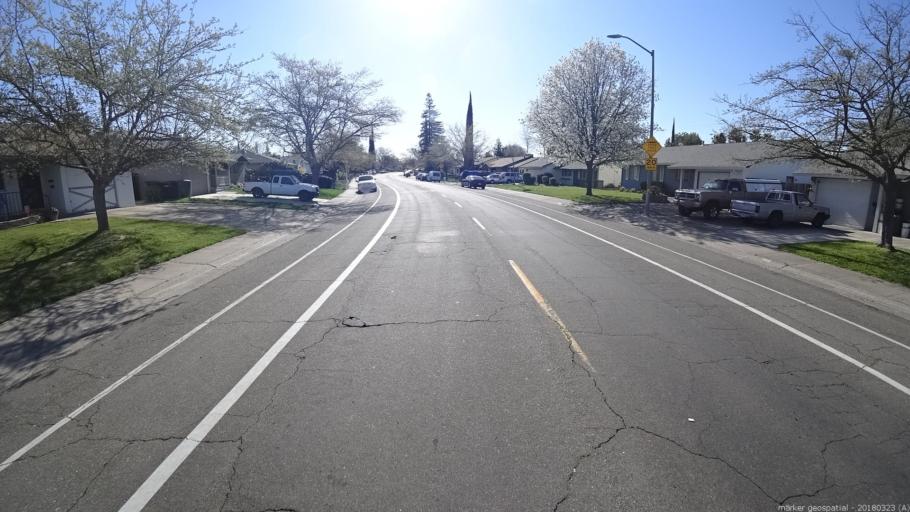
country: US
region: California
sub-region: Sacramento County
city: North Highlands
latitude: 38.6957
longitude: -121.3748
